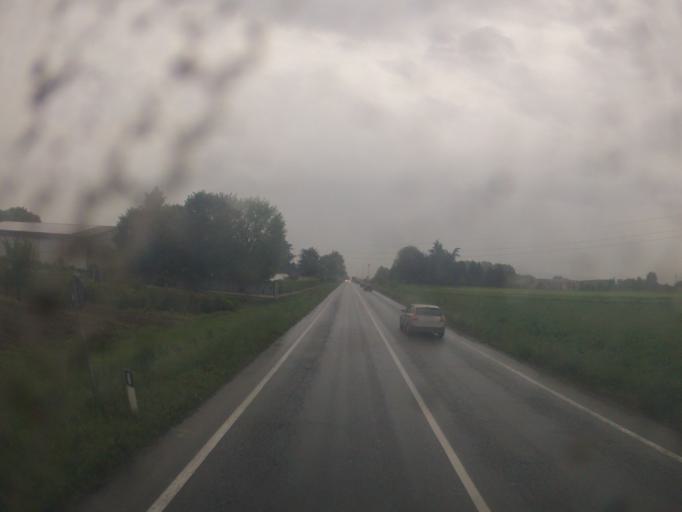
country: IT
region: Piedmont
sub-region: Provincia di Torino
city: La Loggia
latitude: 44.9340
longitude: 7.6716
